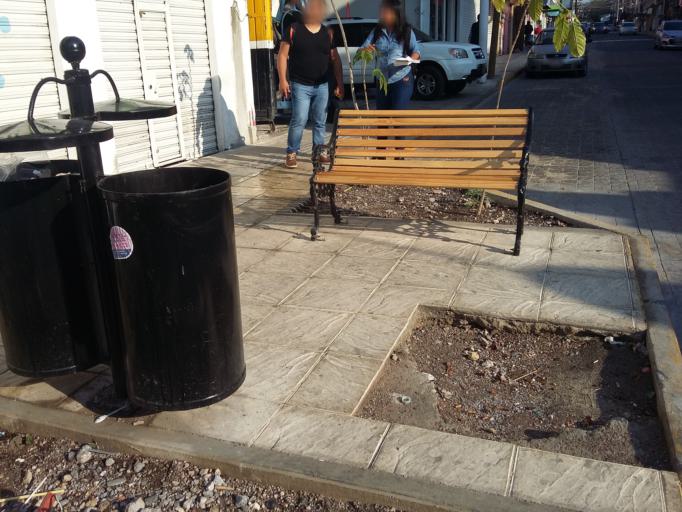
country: MX
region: Guerrero
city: Chilpancingo de los Bravos
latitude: 17.5490
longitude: -99.4997
